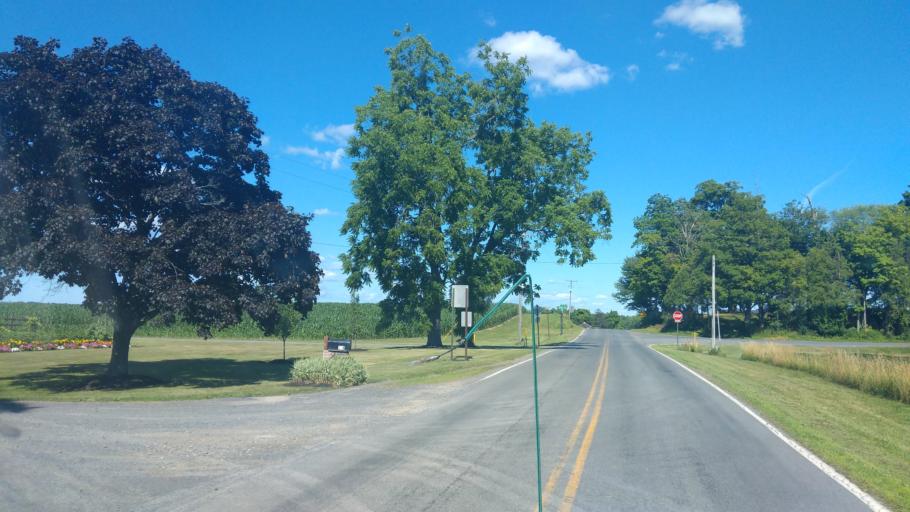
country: US
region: New York
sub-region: Wayne County
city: Clyde
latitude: 43.0203
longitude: -76.8140
